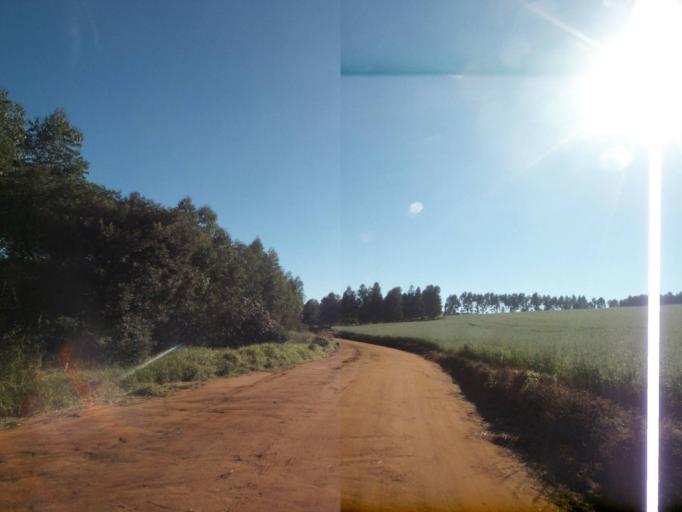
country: BR
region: Parana
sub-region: Tibagi
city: Tibagi
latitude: -24.5408
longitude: -50.3680
